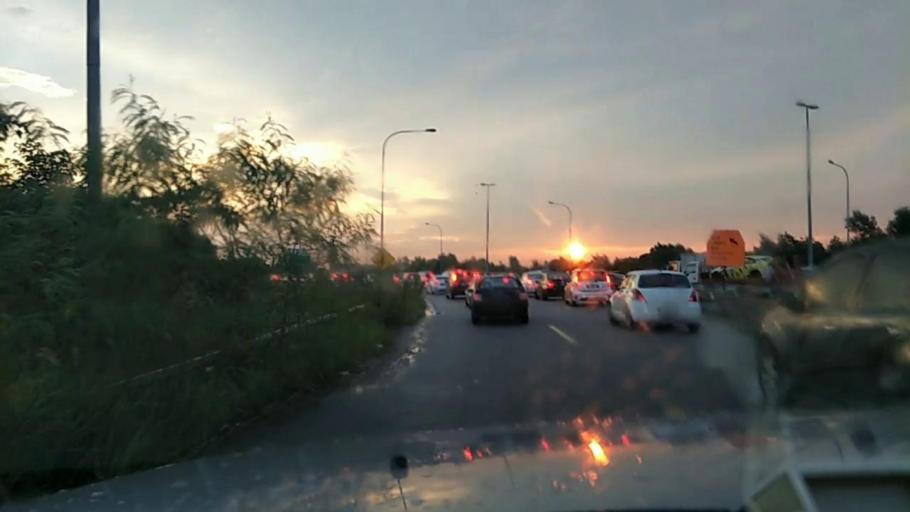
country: MY
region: Putrajaya
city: Putrajaya
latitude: 2.9275
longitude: 101.6207
